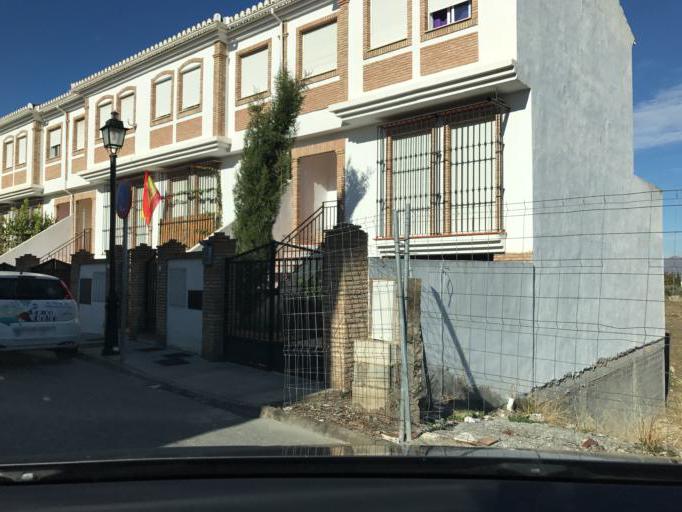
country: ES
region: Andalusia
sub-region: Provincia de Granada
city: Churriana de la Vega
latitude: 37.1400
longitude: -3.6610
